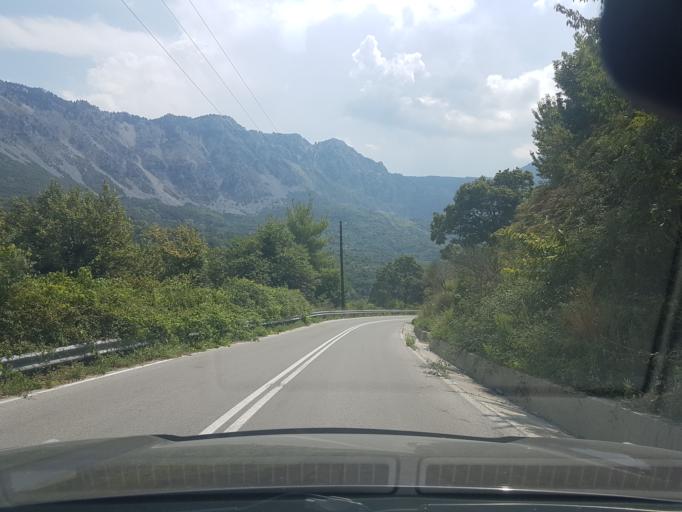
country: GR
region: Central Greece
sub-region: Nomos Evvoias
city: Kymi
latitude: 38.6349
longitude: 23.9454
